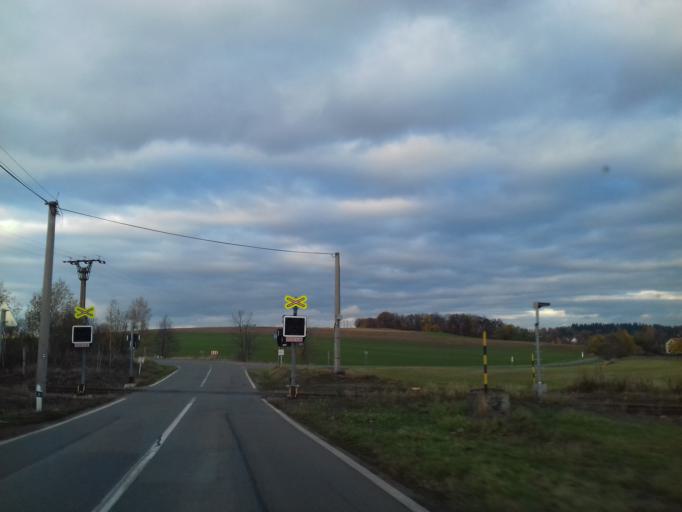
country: CZ
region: Pardubicky
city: Krouna
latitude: 49.7863
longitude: 16.0343
